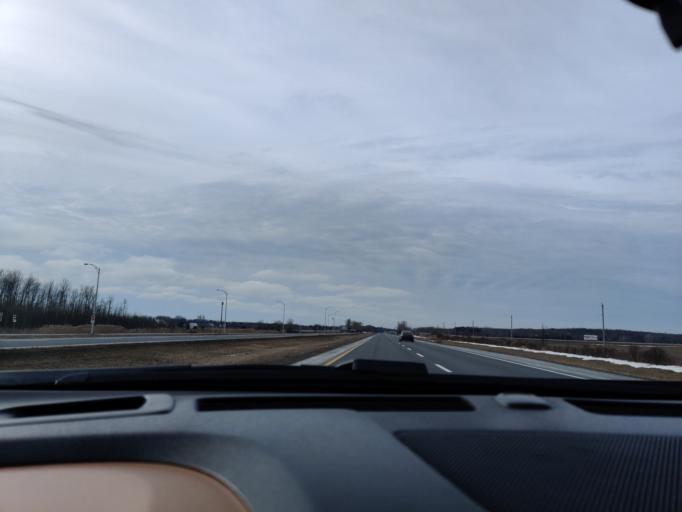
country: CA
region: Quebec
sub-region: Monteregie
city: Les Coteaux
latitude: 45.2132
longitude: -74.3401
